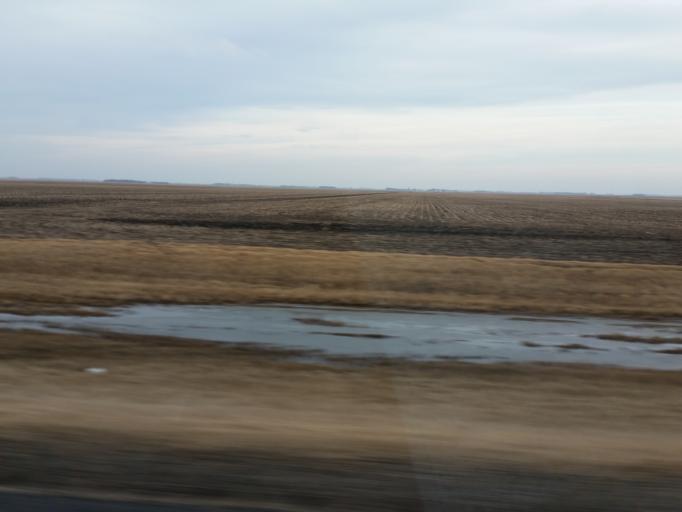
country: US
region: North Dakota
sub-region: Traill County
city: Hillsboro
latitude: 47.2529
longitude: -97.2177
